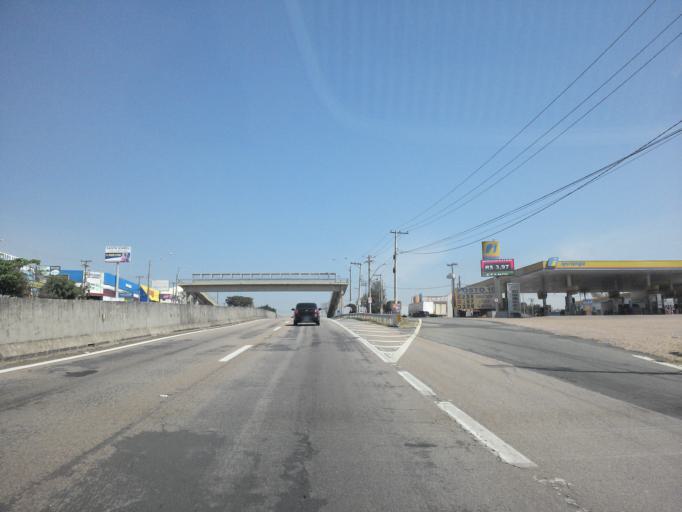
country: BR
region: Sao Paulo
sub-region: Hortolandia
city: Hortolandia
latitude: -22.8921
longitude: -47.1737
